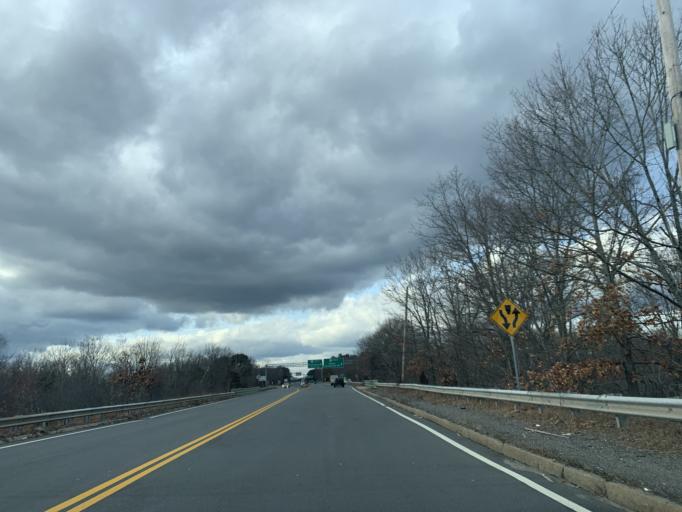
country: US
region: Massachusetts
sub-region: Norfolk County
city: Canton
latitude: 42.1681
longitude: -71.1669
